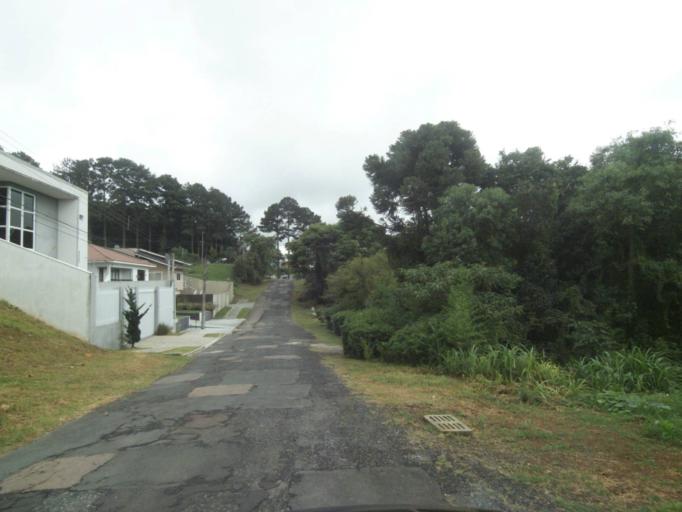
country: BR
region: Parana
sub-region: Curitiba
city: Curitiba
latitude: -25.4676
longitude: -49.3295
